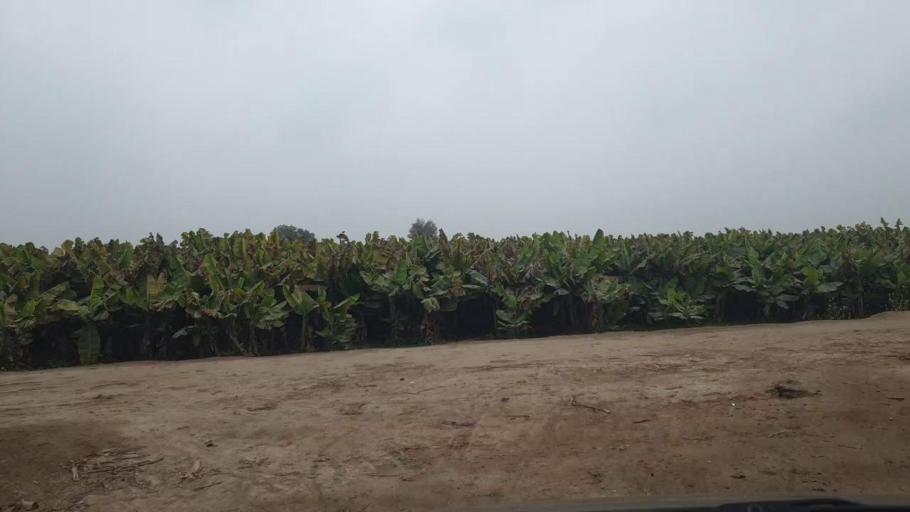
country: PK
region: Sindh
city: Tando Adam
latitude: 25.8317
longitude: 68.7151
